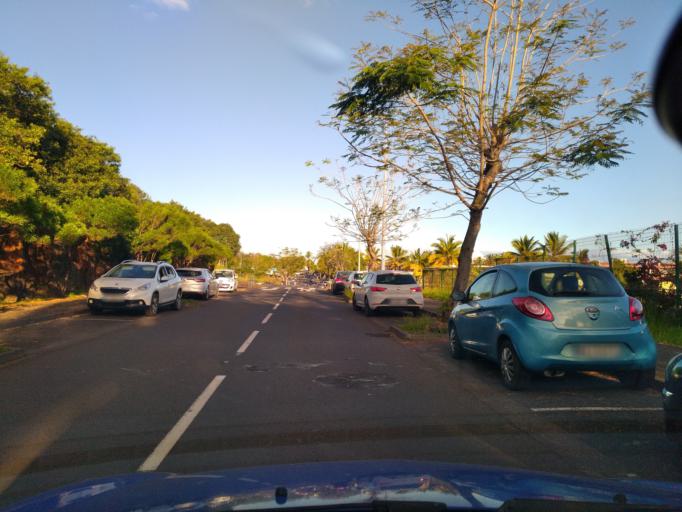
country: RE
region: Reunion
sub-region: Reunion
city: Saint-Pierre
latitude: -21.3418
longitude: 55.4893
